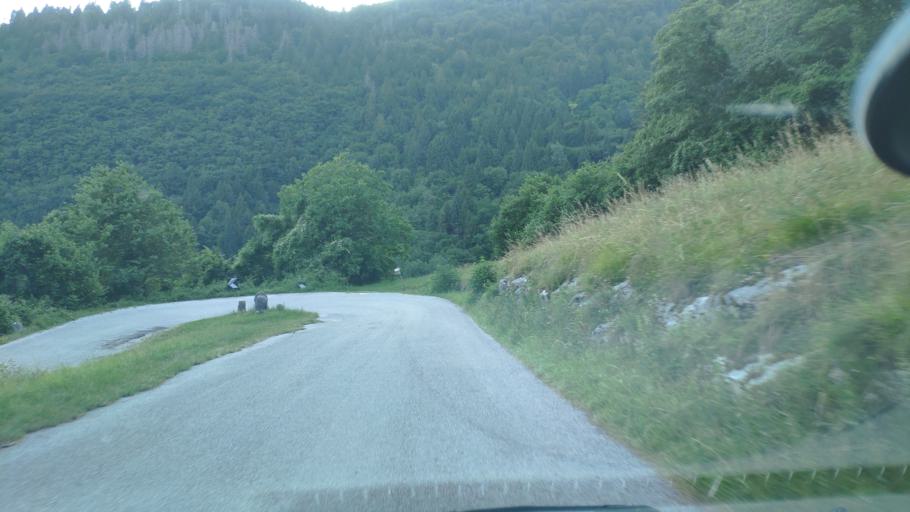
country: IT
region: Veneto
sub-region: Provincia di Vicenza
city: Calvene
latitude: 45.7863
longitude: 11.5077
